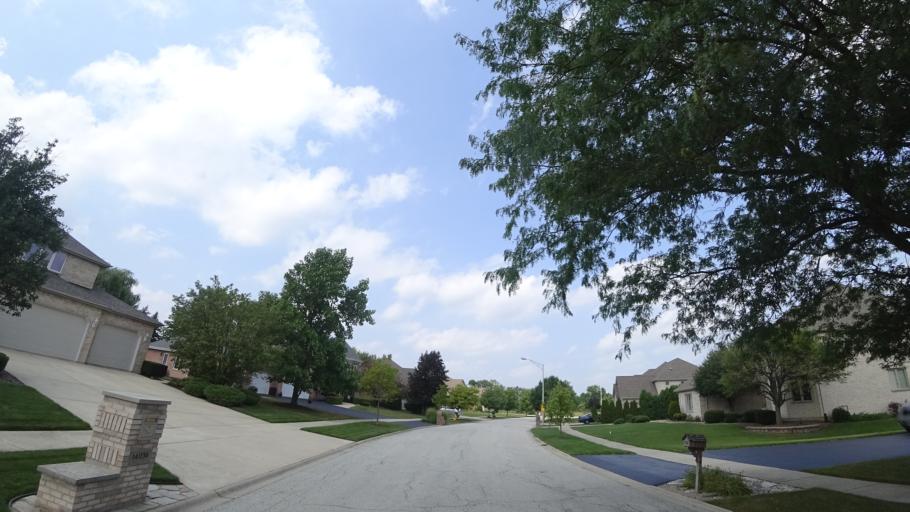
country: US
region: Illinois
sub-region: Cook County
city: Orland Park
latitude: 41.6354
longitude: -87.8909
